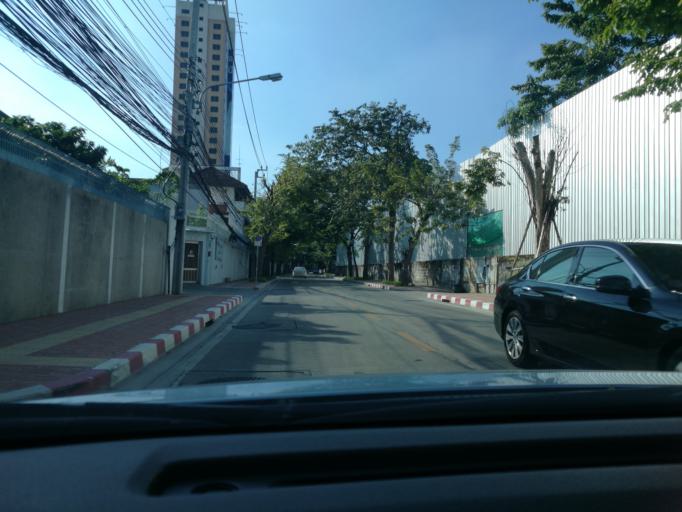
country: TH
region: Bangkok
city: Phaya Thai
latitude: 13.7891
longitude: 100.5398
